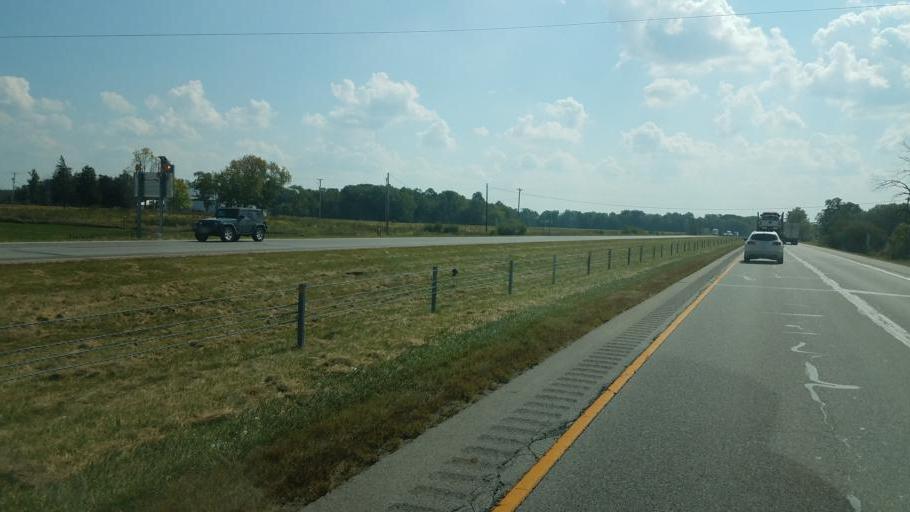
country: US
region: Indiana
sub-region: Allen County
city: Leo-Cedarville
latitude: 41.2668
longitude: -85.0869
